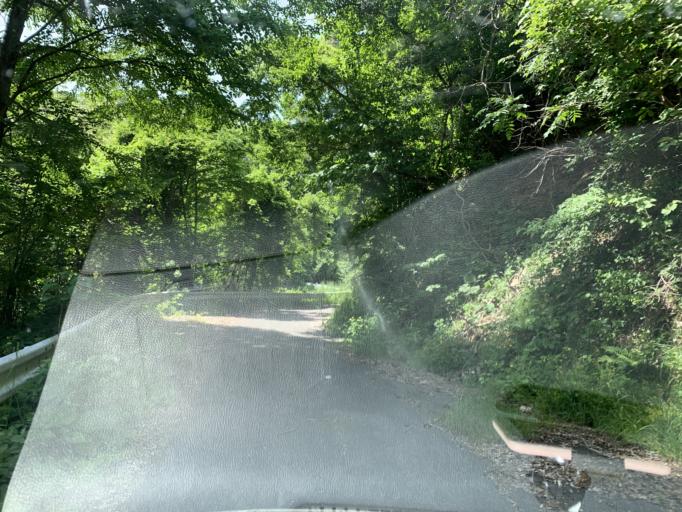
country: JP
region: Iwate
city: Ichinoseki
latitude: 38.9572
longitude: 141.2425
